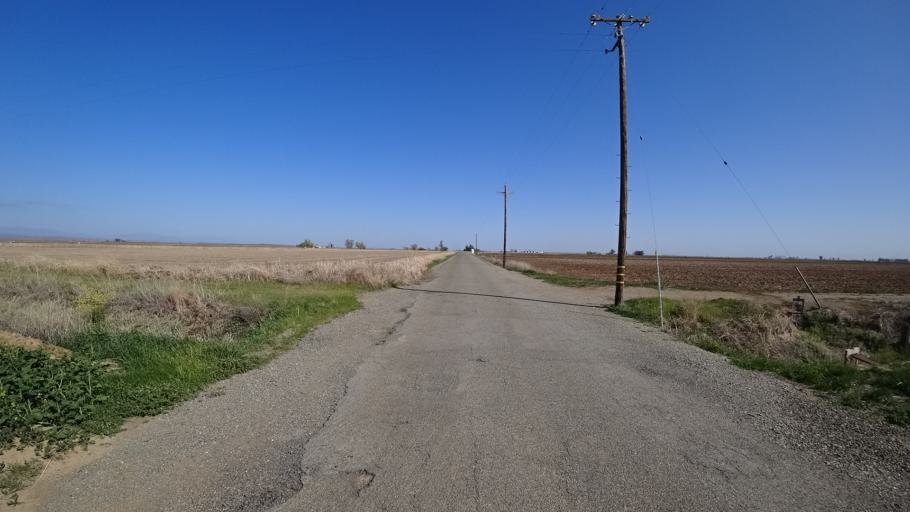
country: US
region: California
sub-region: Glenn County
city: Willows
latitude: 39.4362
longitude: -122.2304
